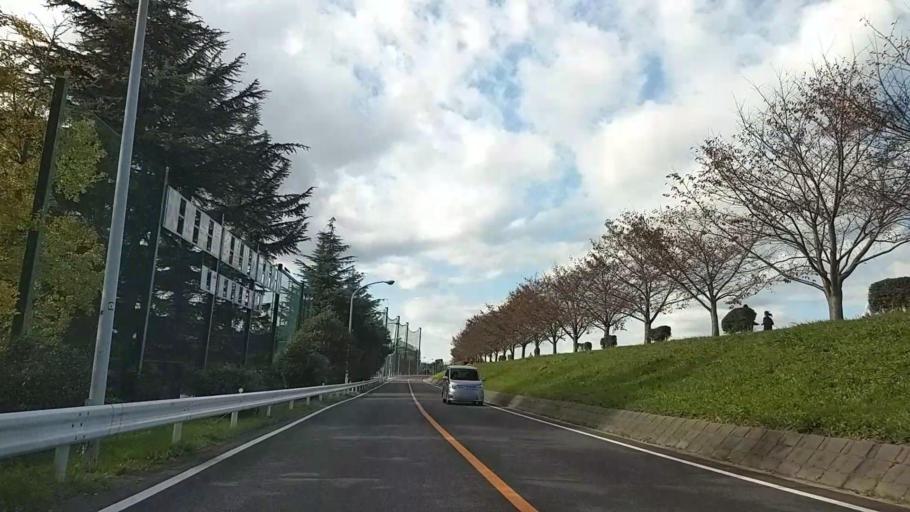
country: JP
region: Kanagawa
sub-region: Kawasaki-shi
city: Kawasaki
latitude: 35.5882
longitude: 139.6571
